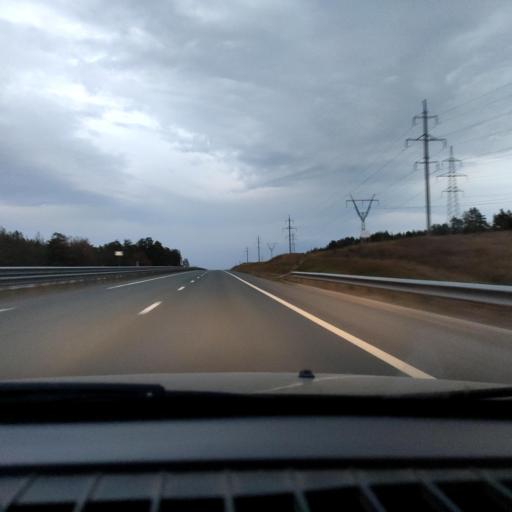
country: RU
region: Samara
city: Povolzhskiy
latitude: 53.5144
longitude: 49.6378
